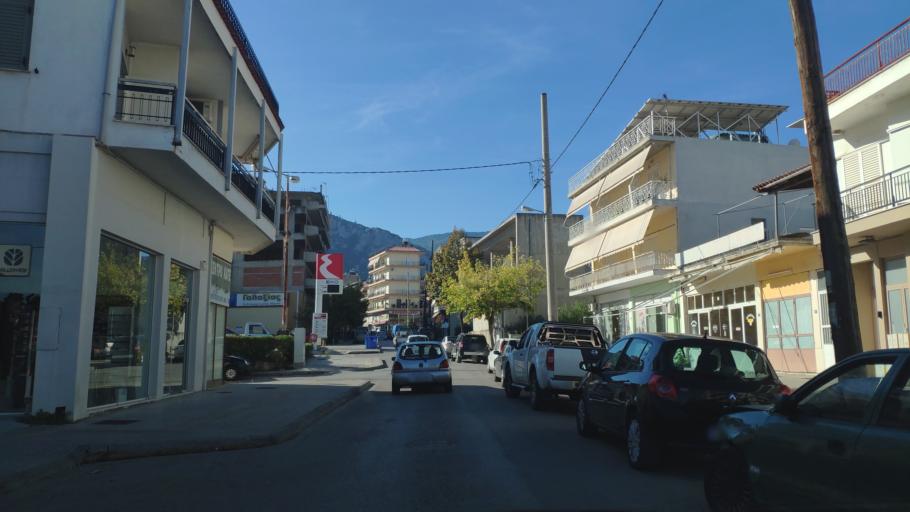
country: GR
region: Central Greece
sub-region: Nomos Voiotias
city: Livadeia
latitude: 38.4413
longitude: 22.8779
